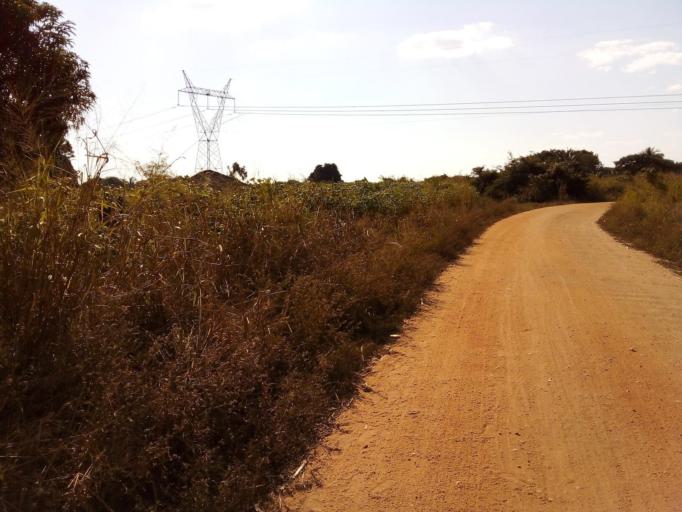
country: MZ
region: Zambezia
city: Quelimane
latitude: -17.5744
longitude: 36.6402
